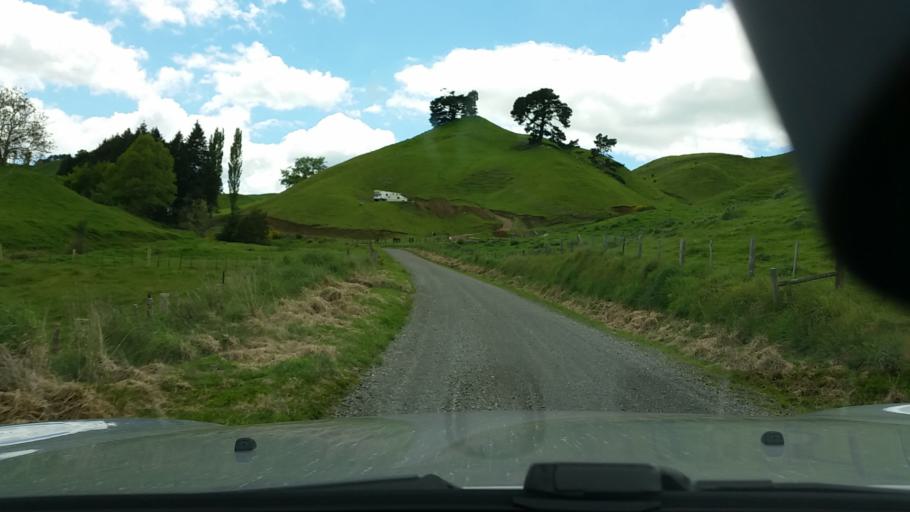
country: NZ
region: Waikato
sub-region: South Waikato District
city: Tokoroa
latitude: -38.3699
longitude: 176.0880
